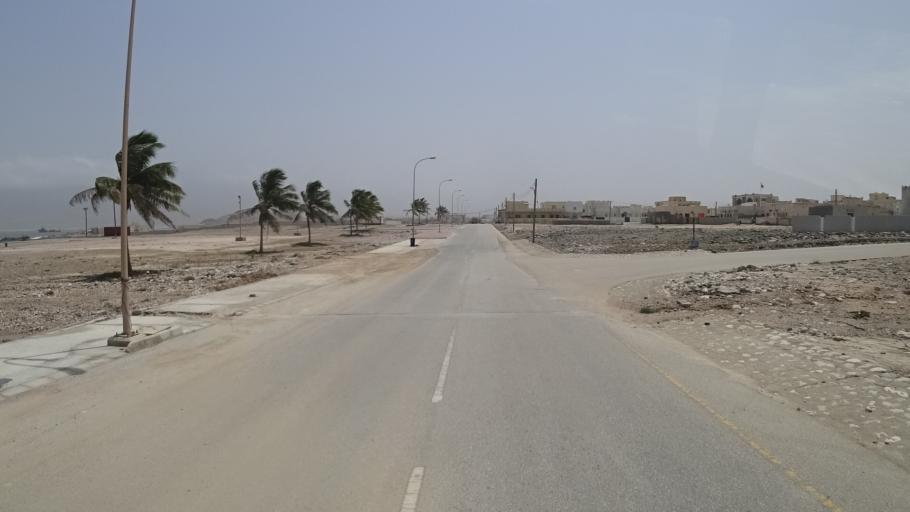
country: OM
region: Zufar
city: Salalah
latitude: 16.9805
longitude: 54.6873
